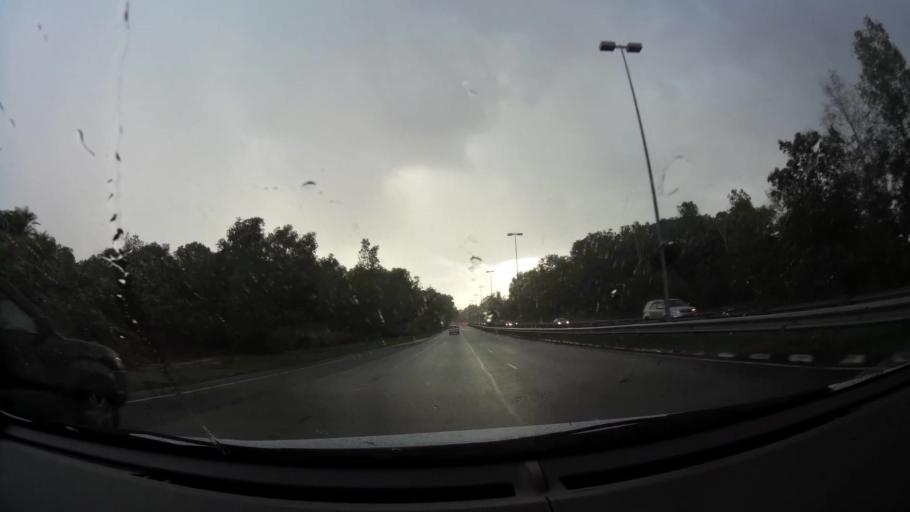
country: BN
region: Brunei and Muara
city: Bandar Seri Begawan
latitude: 4.9264
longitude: 114.9619
